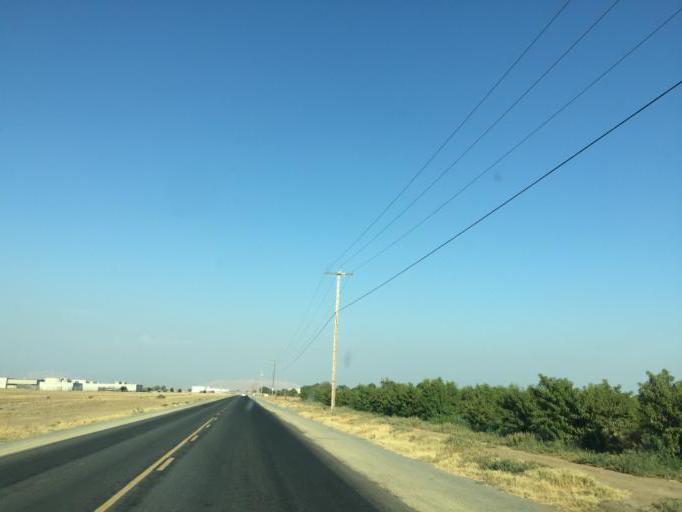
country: US
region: California
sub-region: Tulare County
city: Cutler
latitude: 36.4580
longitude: -119.3315
